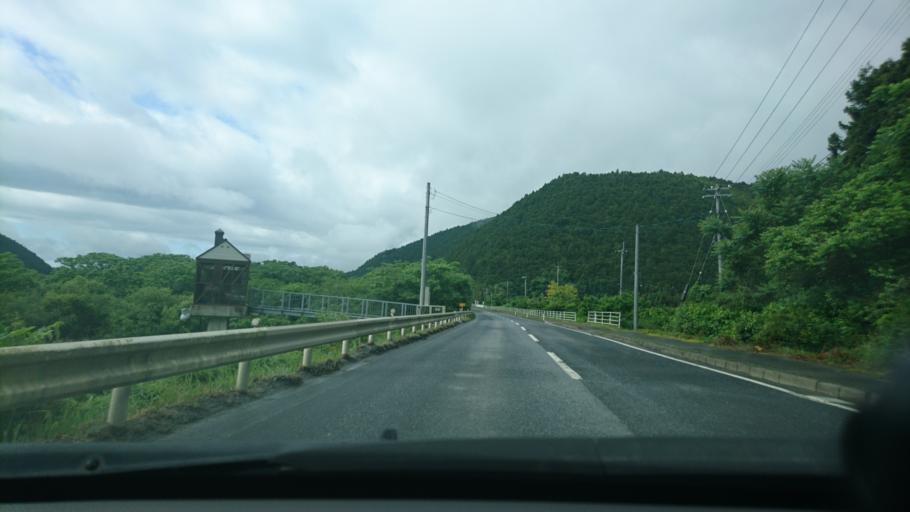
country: JP
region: Miyagi
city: Ishinomaki
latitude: 38.5875
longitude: 141.3041
